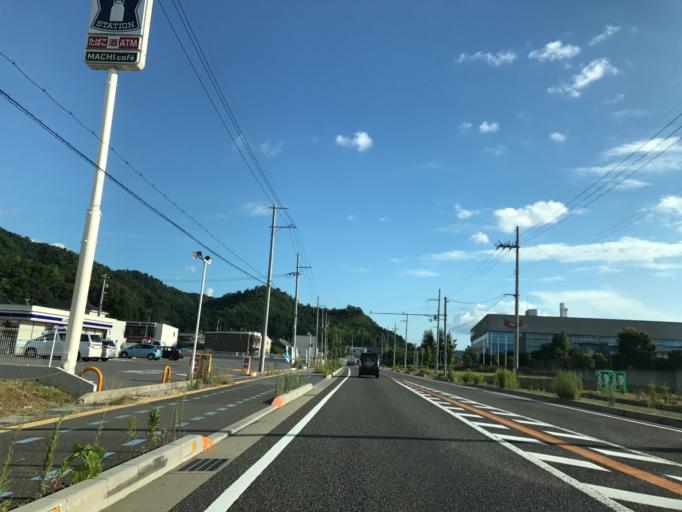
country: JP
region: Shiga Prefecture
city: Hikone
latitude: 35.3091
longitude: 136.2899
